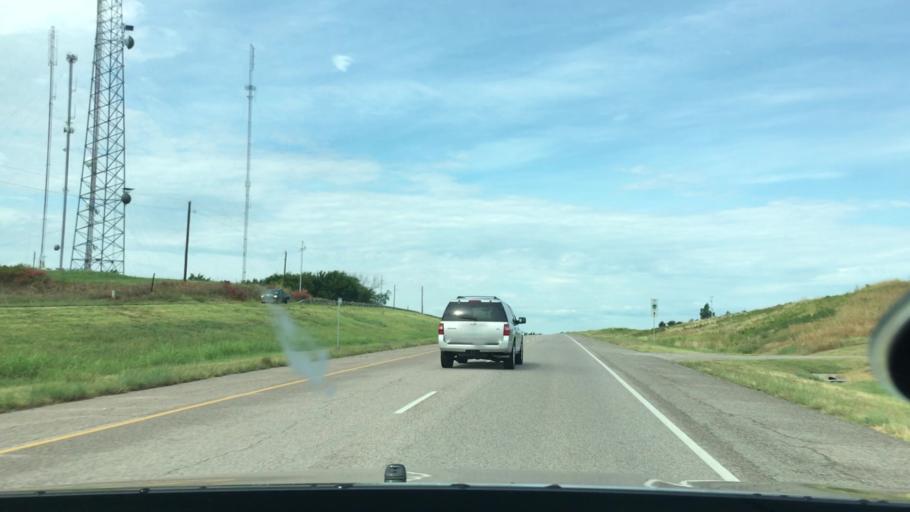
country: US
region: Oklahoma
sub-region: Pontotoc County
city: Ada
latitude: 34.6860
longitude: -96.7592
